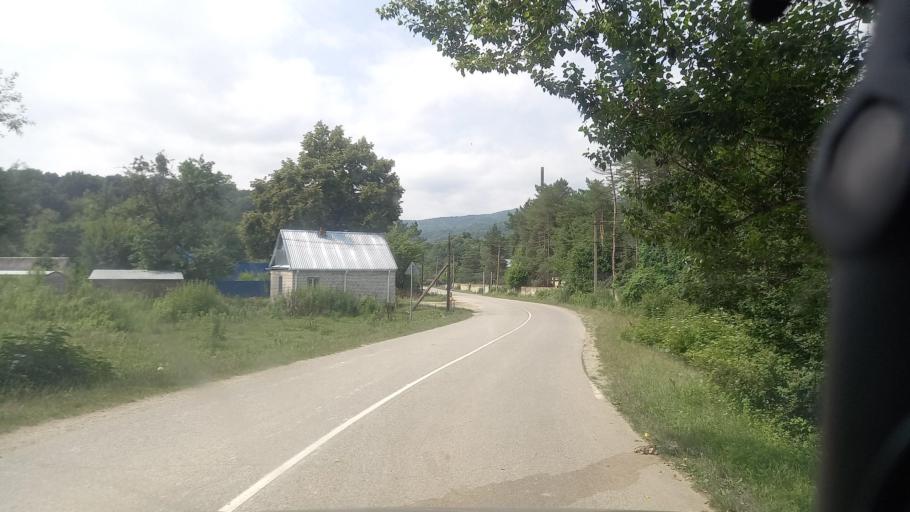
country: RU
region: Karachayevo-Cherkesiya
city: Kurdzhinovo
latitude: 43.9792
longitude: 40.9683
